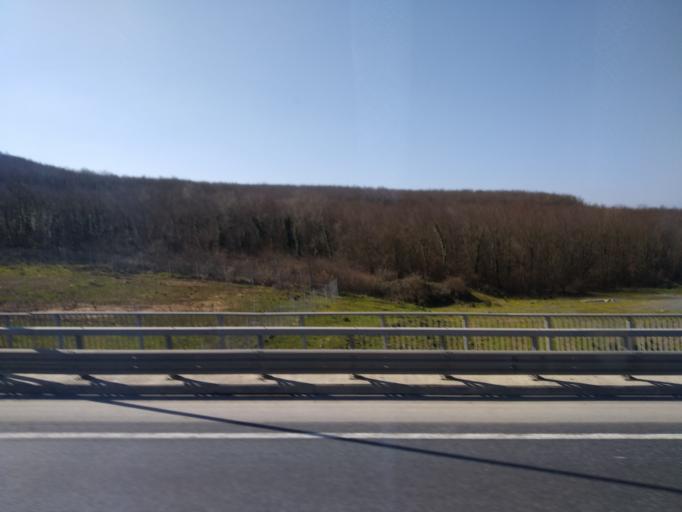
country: TR
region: Istanbul
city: Mahmut Sevket Pasa
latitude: 41.1093
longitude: 29.2926
